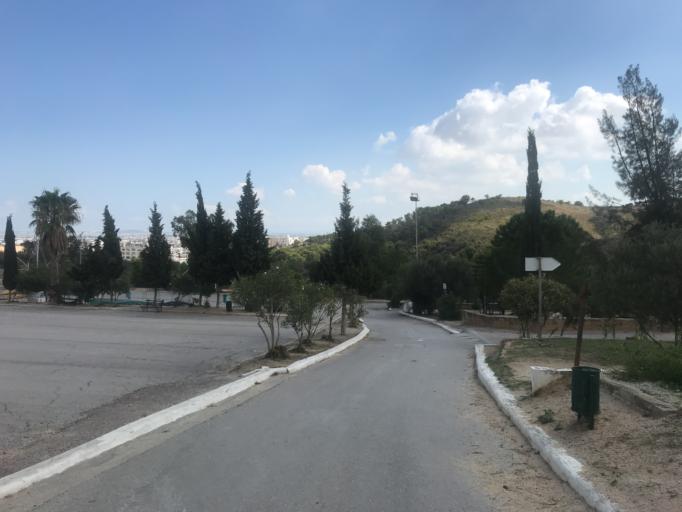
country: TN
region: Ariana
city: Ariana
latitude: 36.8841
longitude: 10.1556
